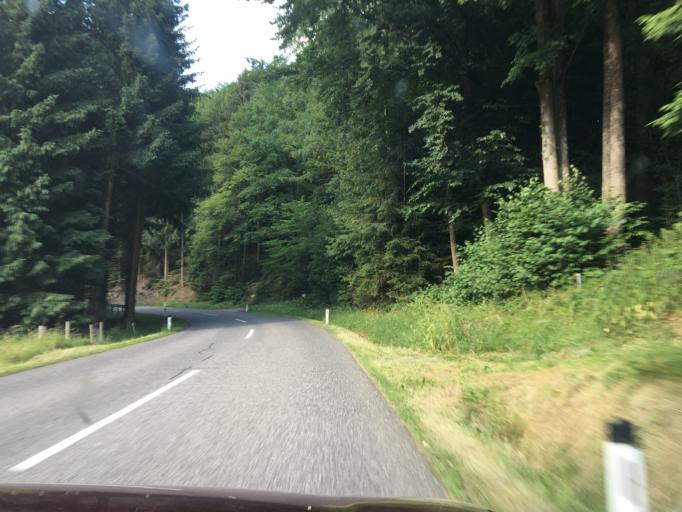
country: AT
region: Upper Austria
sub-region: Politischer Bezirk Urfahr-Umgebung
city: Alberndorf in der Riedmark
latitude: 48.4025
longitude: 14.3979
